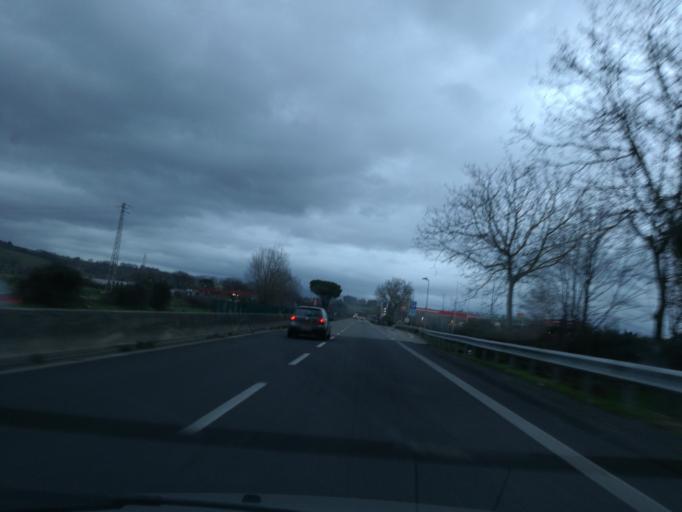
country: IT
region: Umbria
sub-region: Provincia di Perugia
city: Ponte Felcino
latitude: 43.1087
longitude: 12.4633
